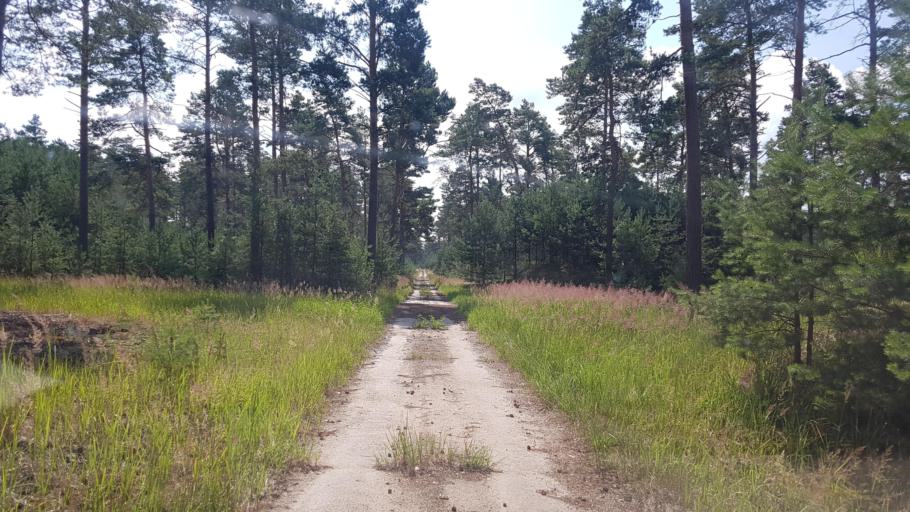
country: DE
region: Brandenburg
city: Crinitz
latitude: 51.7075
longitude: 13.7390
